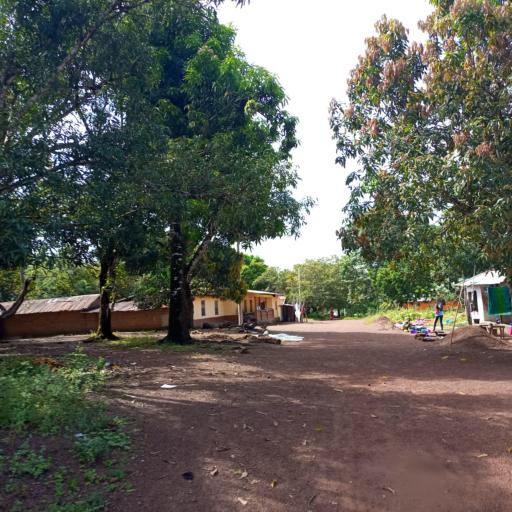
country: SL
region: Northern Province
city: Kambia
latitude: 9.1207
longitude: -12.9146
